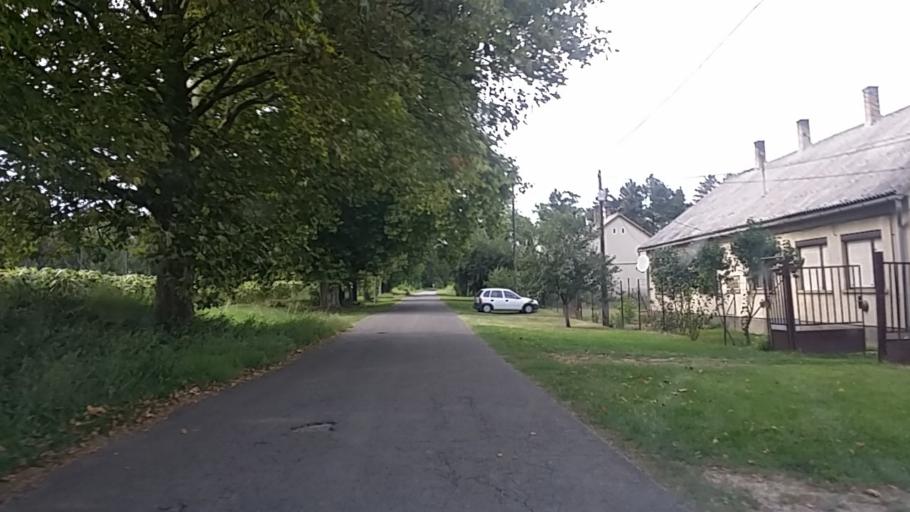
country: HU
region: Tolna
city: Szedres
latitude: 46.5285
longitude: 18.6376
